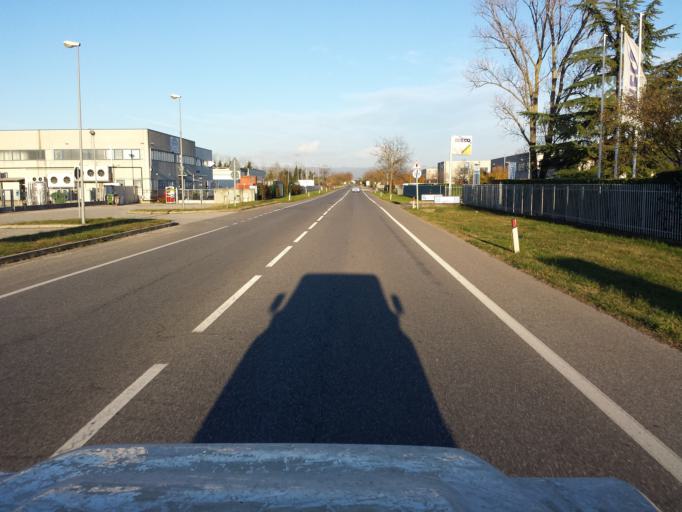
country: IT
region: Friuli Venezia Giulia
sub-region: Provincia di Gorizia
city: Villesse
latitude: 45.8729
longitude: 13.4541
